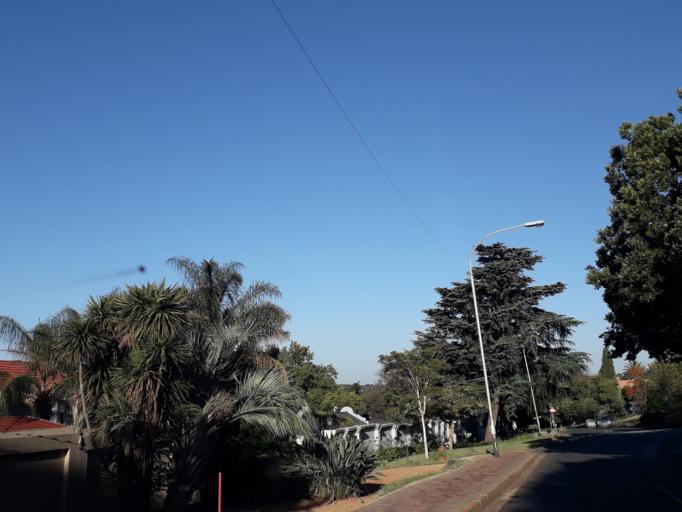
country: ZA
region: Gauteng
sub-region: City of Johannesburg Metropolitan Municipality
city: Johannesburg
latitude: -26.1393
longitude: 27.9726
